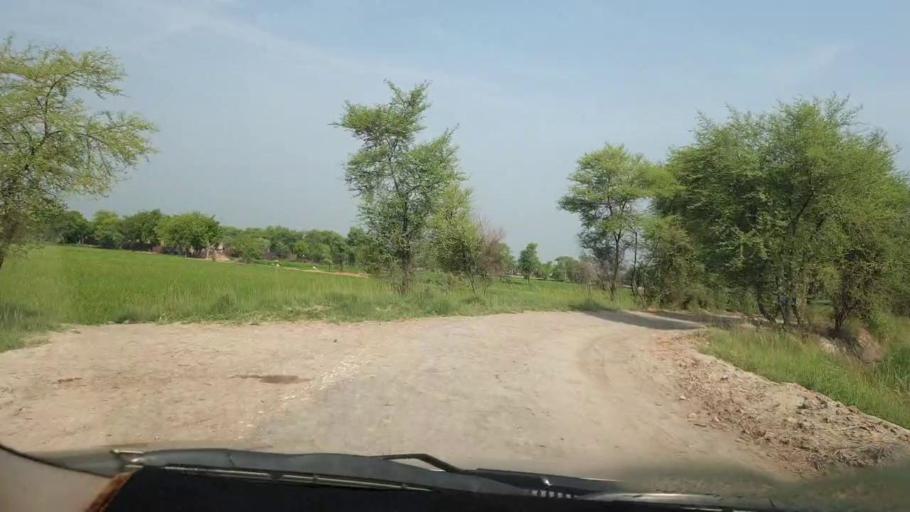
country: PK
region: Sindh
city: Goth Garelo
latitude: 27.4511
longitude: 68.0204
